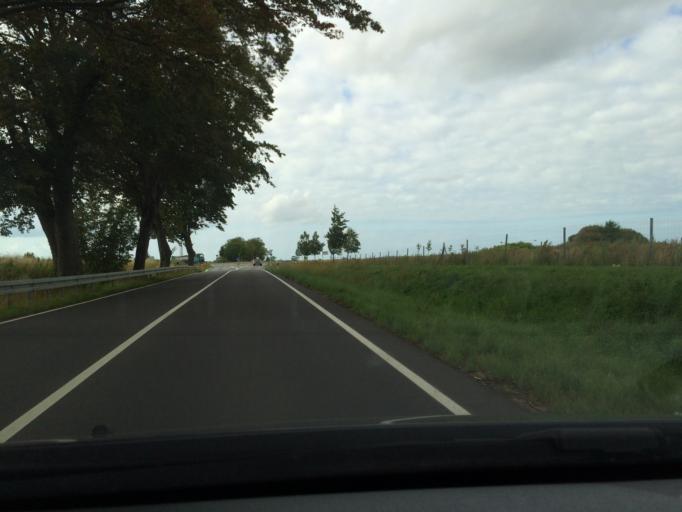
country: DE
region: Mecklenburg-Vorpommern
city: Kramerhof
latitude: 54.3501
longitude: 13.0441
